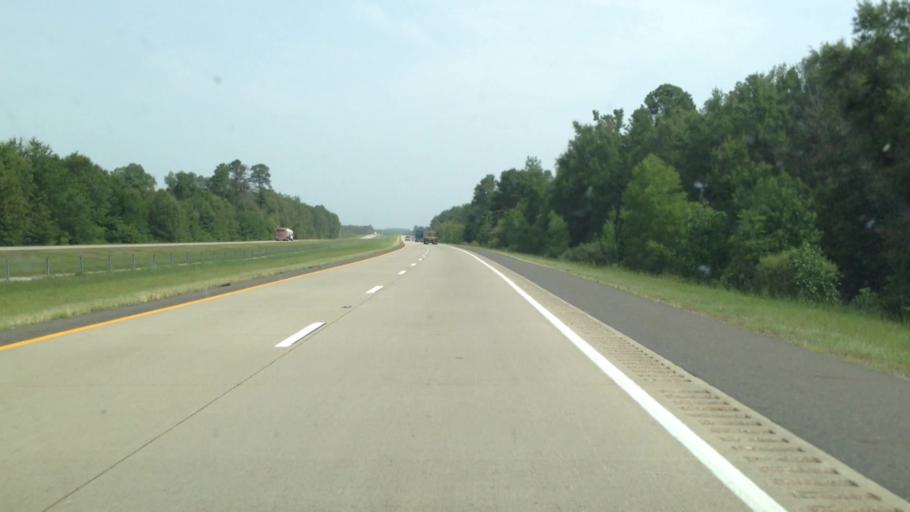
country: US
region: Texas
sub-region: Bowie County
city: Texarkana
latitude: 33.2144
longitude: -93.8736
